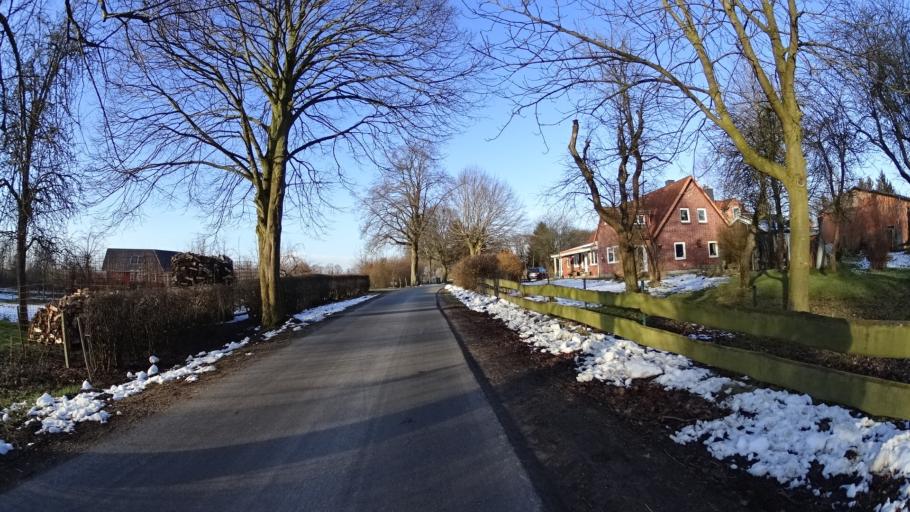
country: DE
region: Schleswig-Holstein
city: Fargau-Pratjau
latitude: 54.3429
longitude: 10.4089
